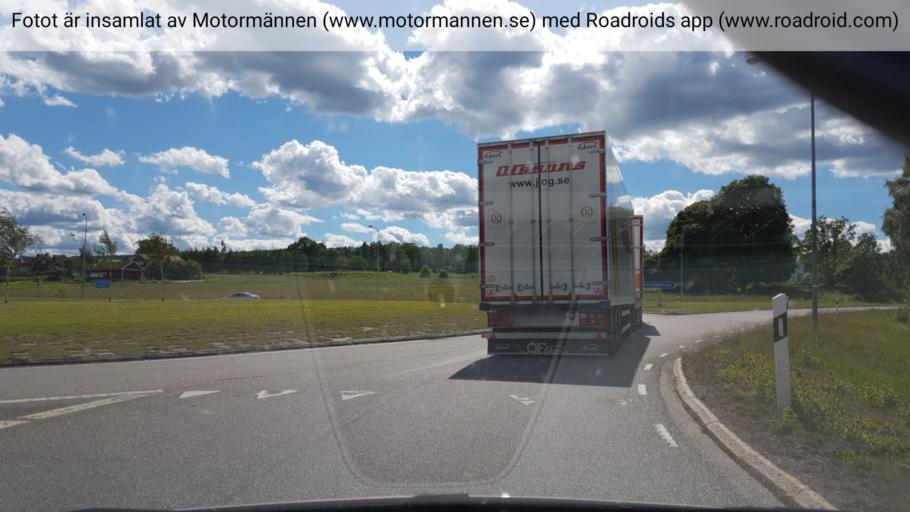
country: SE
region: Vaestra Goetaland
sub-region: Hjo Kommun
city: Hjo
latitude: 58.3041
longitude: 14.2552
